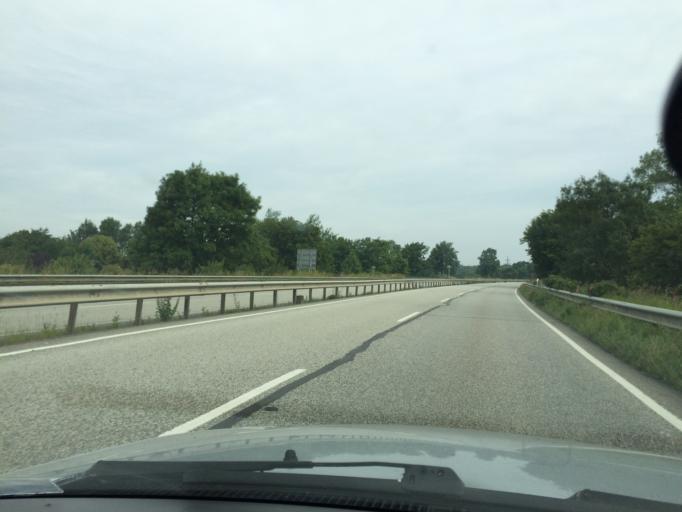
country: DE
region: Schleswig-Holstein
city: Harrislee
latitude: 54.7813
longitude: 9.4056
